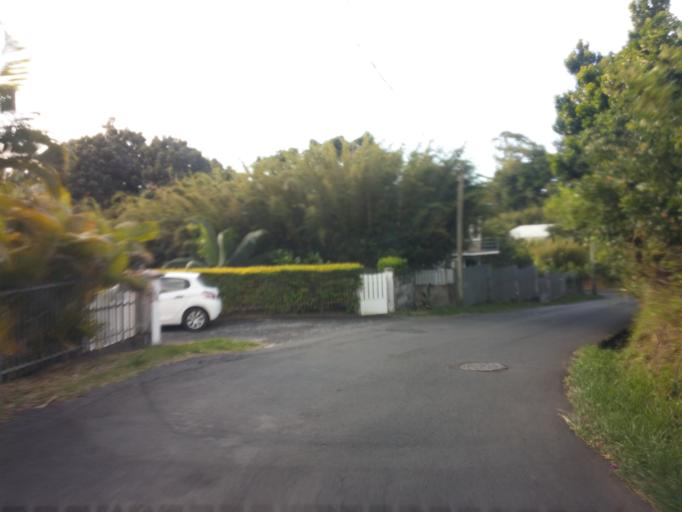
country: RE
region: Reunion
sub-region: Reunion
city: Saint-Denis
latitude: -20.8861
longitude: 55.4285
